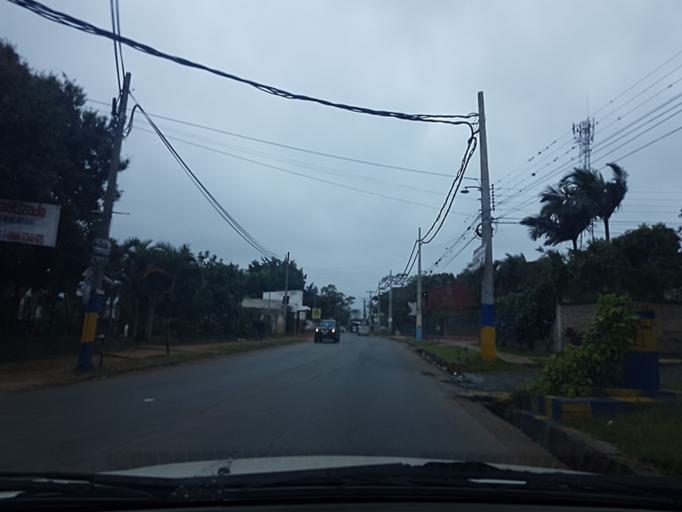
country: PY
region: Central
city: San Lorenzo
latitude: -25.2705
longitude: -57.4781
